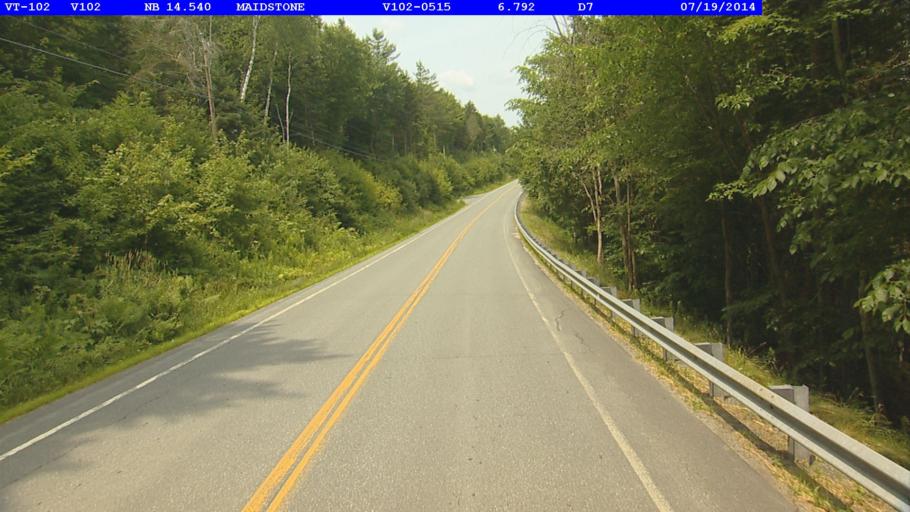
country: US
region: New Hampshire
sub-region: Coos County
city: Stratford
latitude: 44.6511
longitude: -71.5809
